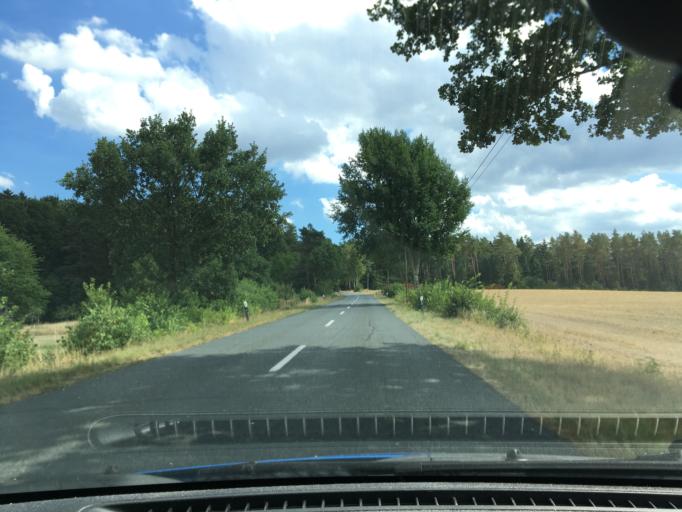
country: DE
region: Lower Saxony
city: Rehlingen
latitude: 53.0865
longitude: 10.2074
